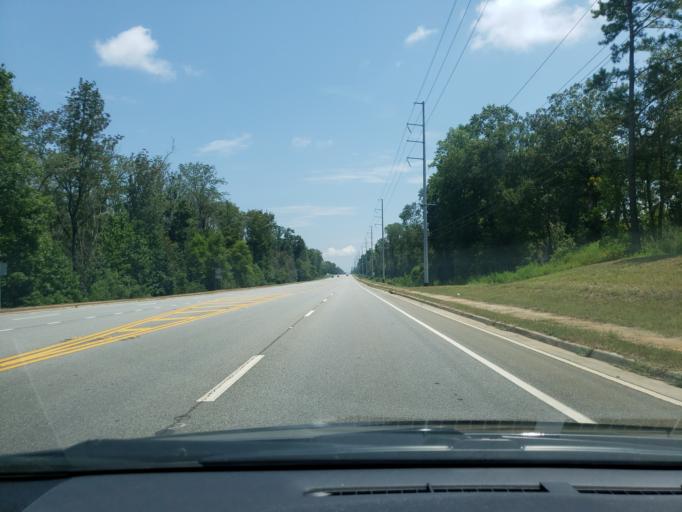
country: US
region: Georgia
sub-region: Dougherty County
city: Albany
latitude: 31.5856
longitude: -84.2694
